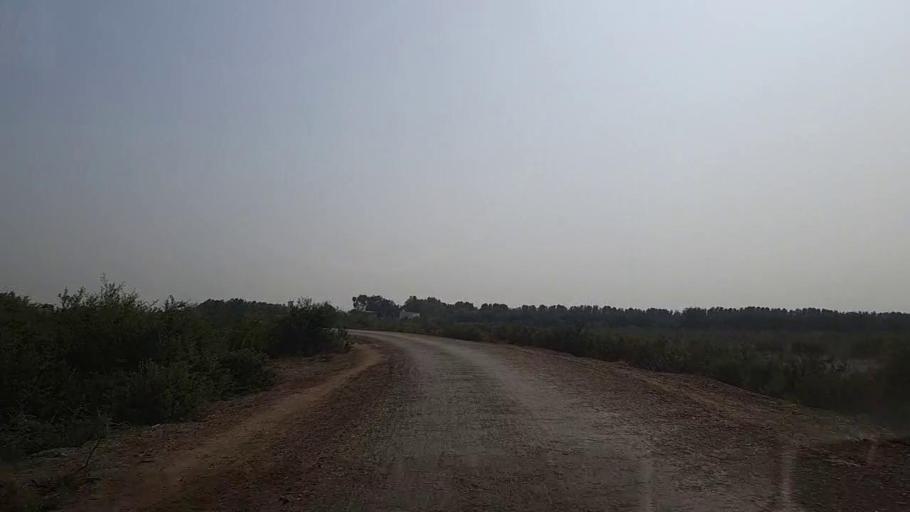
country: PK
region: Sindh
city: Keti Bandar
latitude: 24.2263
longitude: 67.6652
